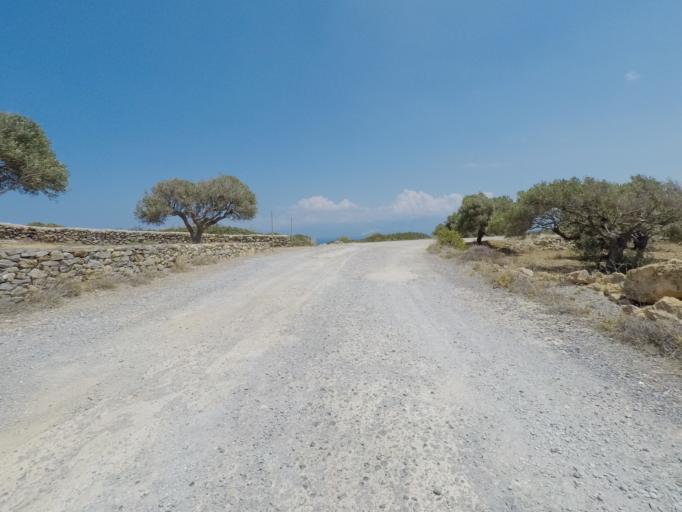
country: GR
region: Crete
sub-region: Nomos Lasithiou
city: Elounda
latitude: 35.3173
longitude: 25.7480
